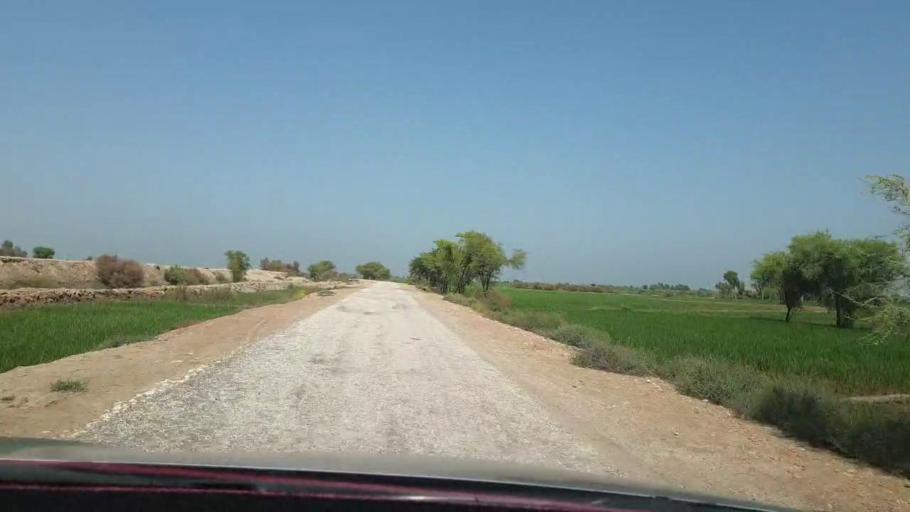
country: PK
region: Sindh
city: Warah
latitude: 27.5507
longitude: 67.7375
